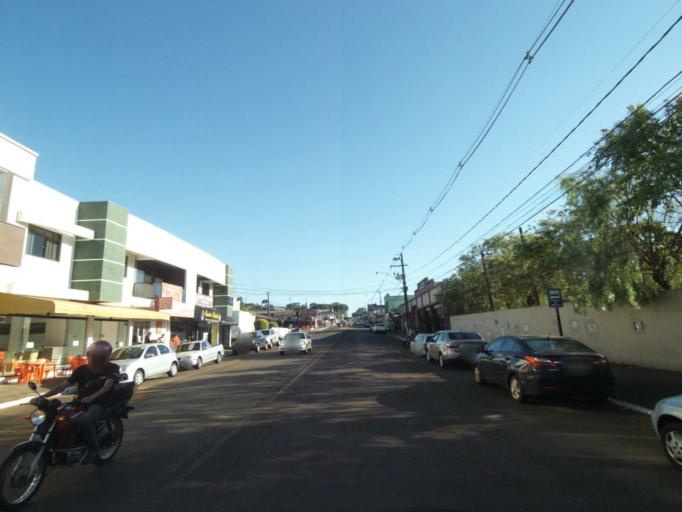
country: BR
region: Parana
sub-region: Coronel Vivida
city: Coronel Vivida
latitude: -25.9682
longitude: -52.8145
